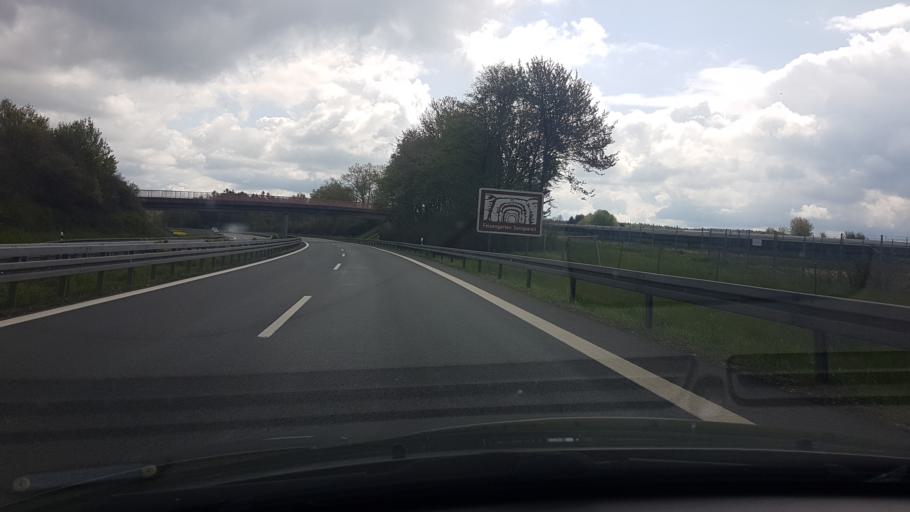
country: DE
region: Bavaria
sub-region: Upper Franconia
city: Wonsees
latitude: 50.0049
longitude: 11.2895
